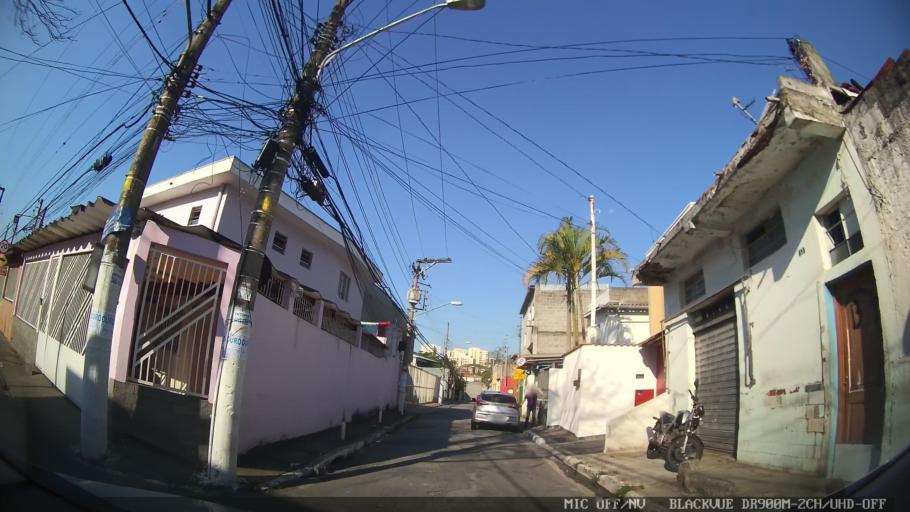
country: BR
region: Sao Paulo
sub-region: Sao Paulo
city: Sao Paulo
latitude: -23.5082
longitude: -46.6687
